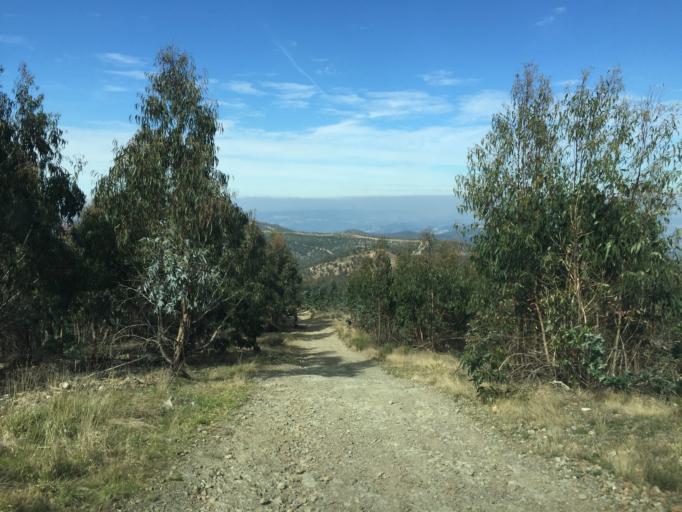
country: PT
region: Aveiro
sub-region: Arouca
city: Arouca
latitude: 40.9653
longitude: -8.2399
